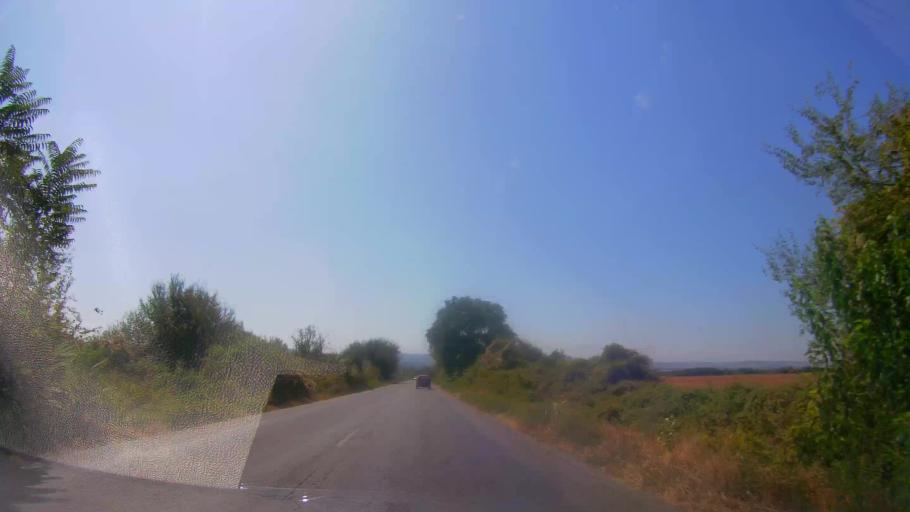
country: BG
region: Veliko Turnovo
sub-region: Obshtina Gorna Oryakhovitsa
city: Purvomaytsi
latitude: 43.2274
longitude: 25.6389
